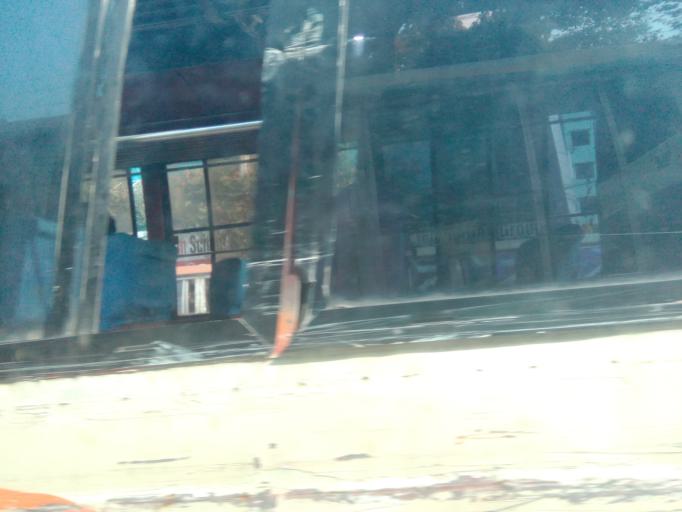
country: BD
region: Dhaka
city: Paltan
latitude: 23.7940
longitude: 90.4243
